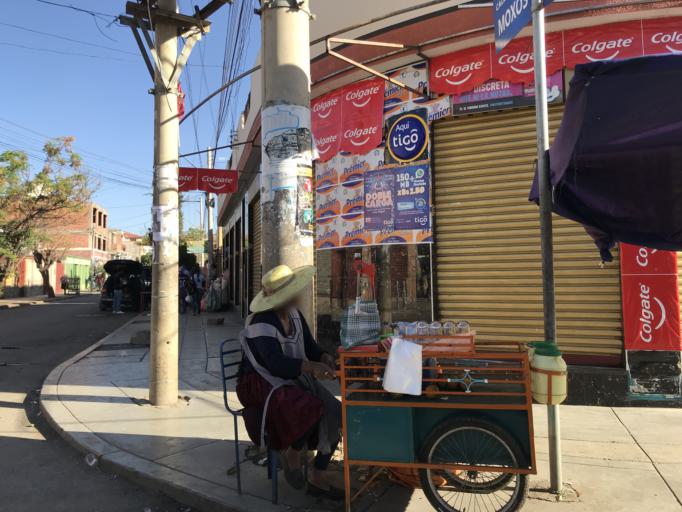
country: BO
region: Cochabamba
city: Cochabamba
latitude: -17.4075
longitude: -66.1503
